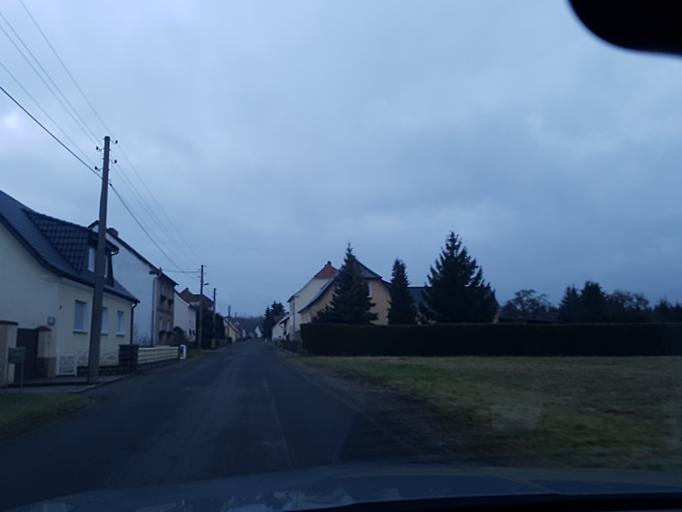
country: DE
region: Brandenburg
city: Schonborn
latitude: 51.5969
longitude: 13.4914
